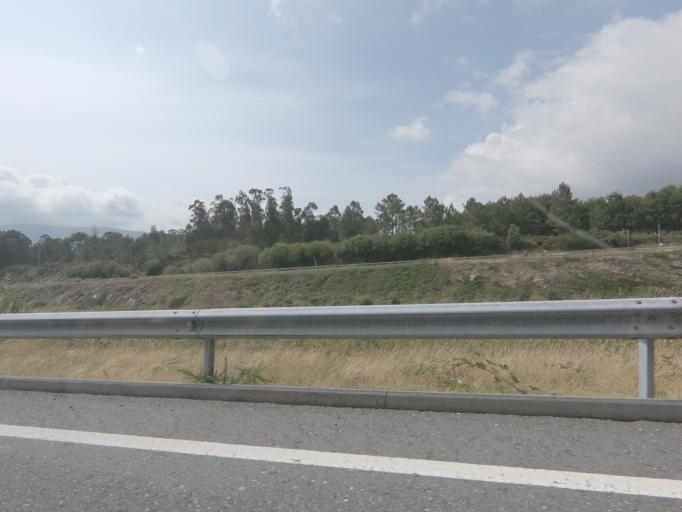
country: ES
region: Galicia
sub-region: Provincia de Ourense
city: Melon
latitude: 42.2049
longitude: -8.2685
